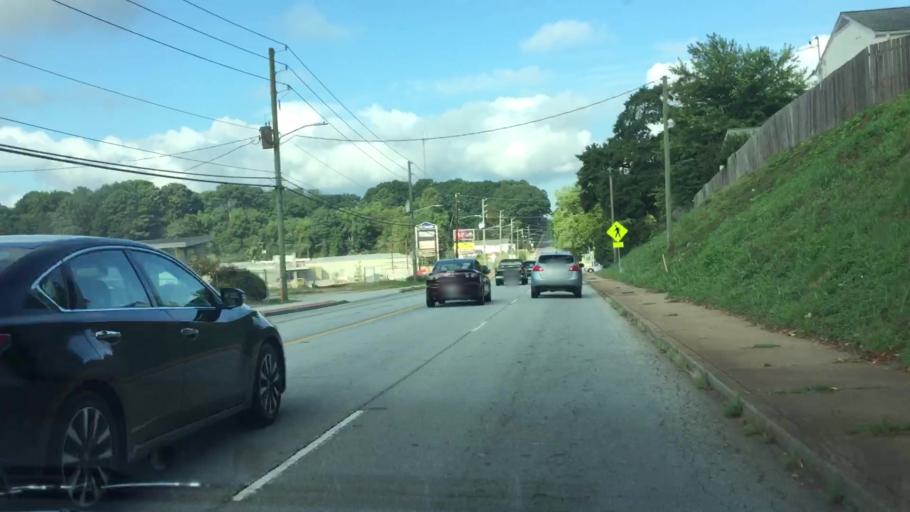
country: US
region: Georgia
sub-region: DeKalb County
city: Druid Hills
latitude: 33.7475
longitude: -84.3342
